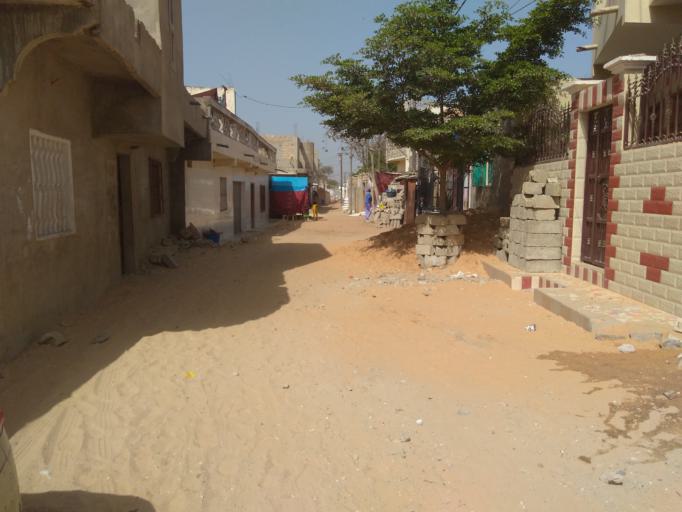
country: SN
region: Dakar
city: Pikine
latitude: 14.7942
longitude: -17.3370
